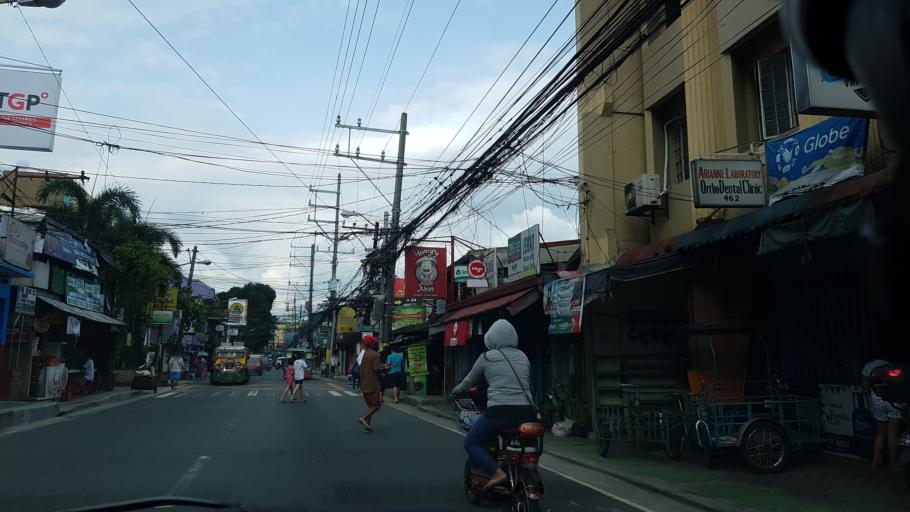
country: PH
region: Metro Manila
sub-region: Pasig
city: Pasig City
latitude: 14.5780
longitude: 121.0815
